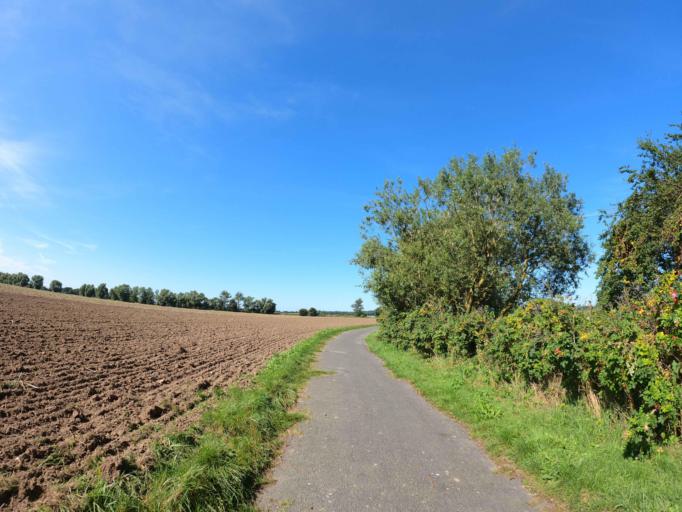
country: DE
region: Mecklenburg-Vorpommern
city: Prohn
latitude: 54.3906
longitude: 13.0335
